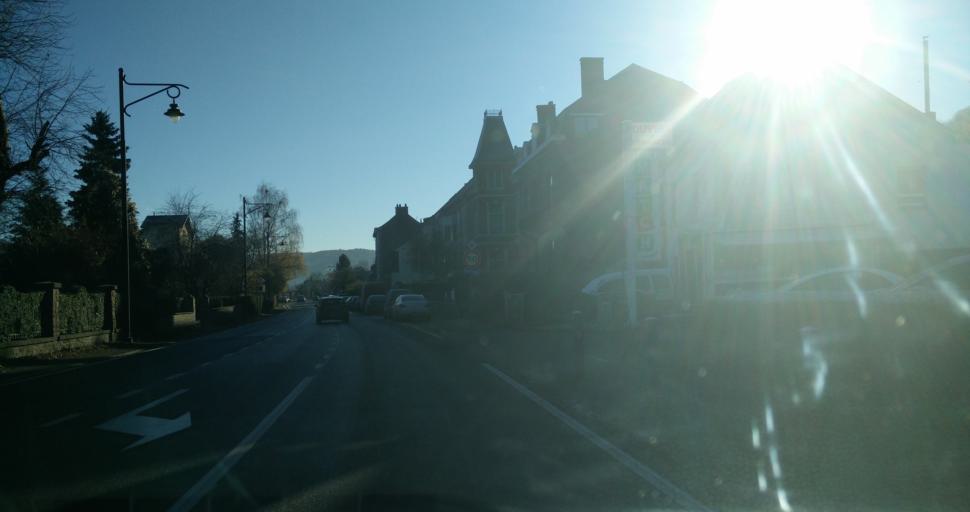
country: BE
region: Wallonia
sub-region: Province de Namur
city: Namur
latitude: 50.4284
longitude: 4.8668
